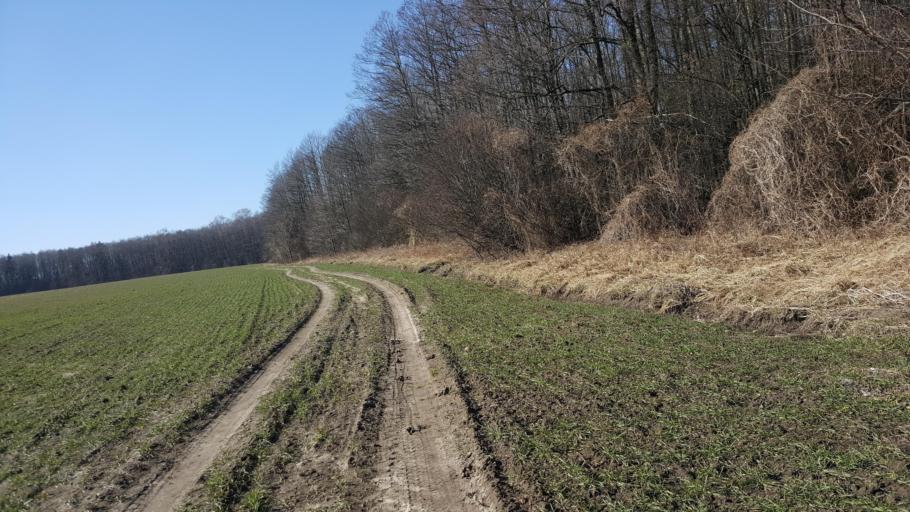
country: BY
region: Brest
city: Kamyanyets
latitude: 52.3665
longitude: 23.7696
